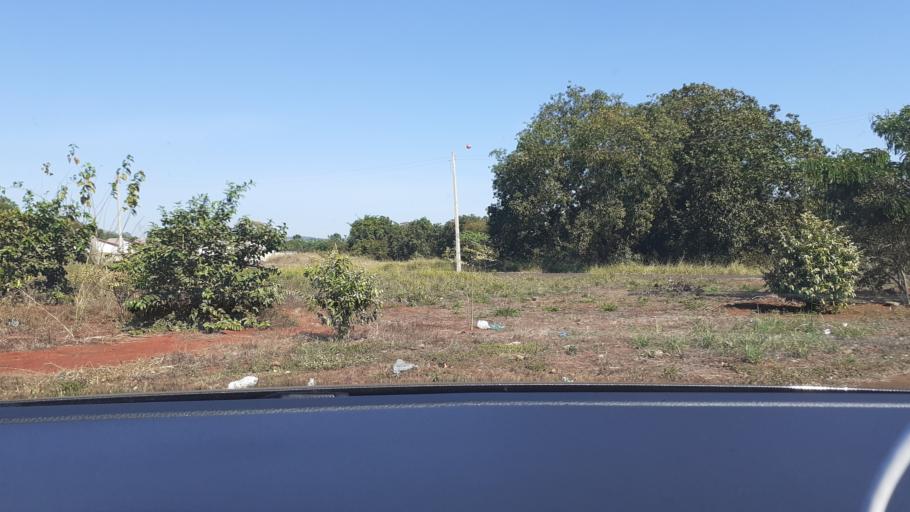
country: BR
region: Goias
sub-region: Itumbiara
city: Itumbiara
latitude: -18.4112
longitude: -49.2582
